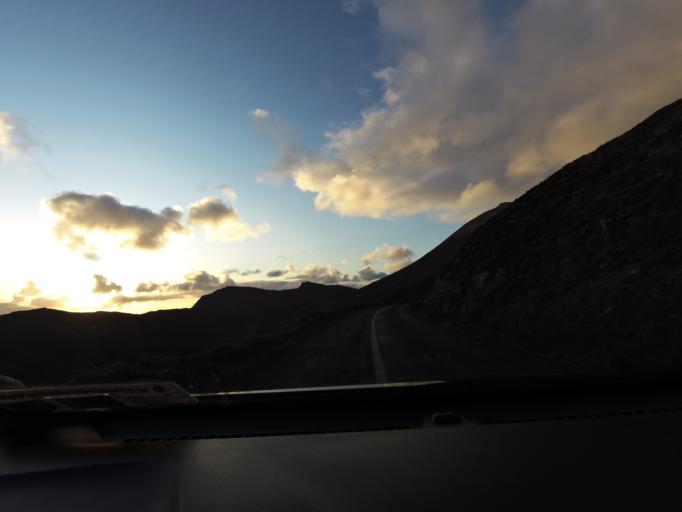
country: IE
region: Connaught
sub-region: Maigh Eo
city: Belmullet
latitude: 53.9703
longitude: -10.1790
